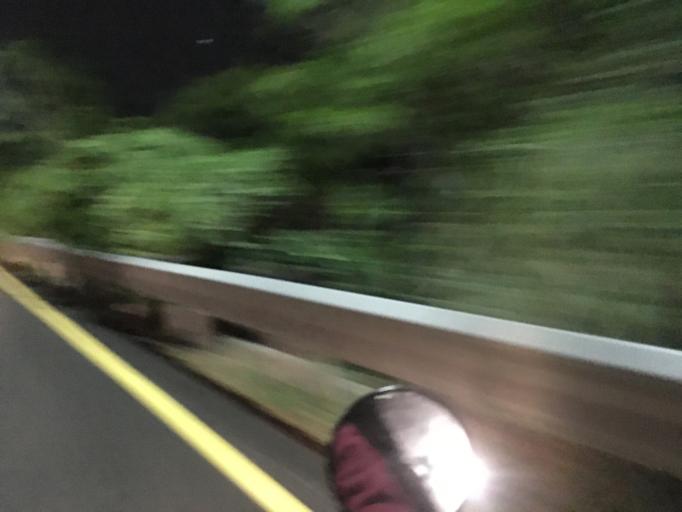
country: TW
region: Taiwan
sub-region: Hsinchu
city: Hsinchu
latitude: 24.7674
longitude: 120.9545
